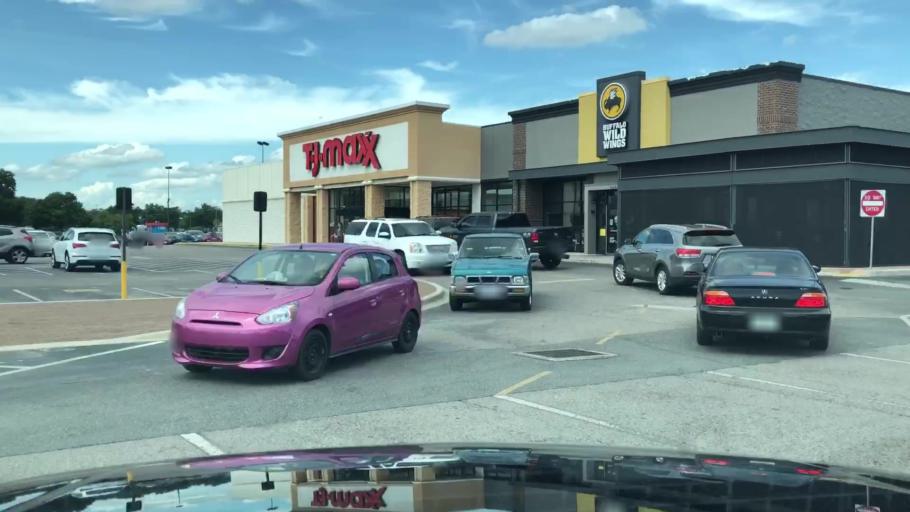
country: US
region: Florida
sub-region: Columbia County
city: Lake City
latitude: 30.1799
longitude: -82.6723
